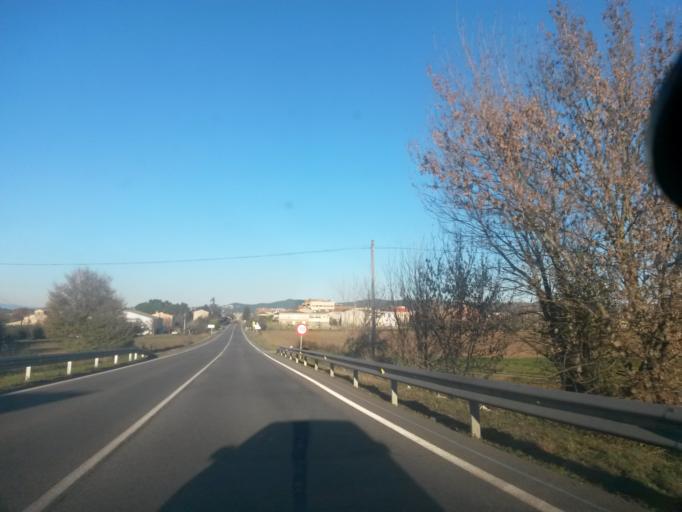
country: ES
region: Catalonia
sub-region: Provincia de Girona
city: Vilablareix
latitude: 41.9473
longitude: 2.7901
